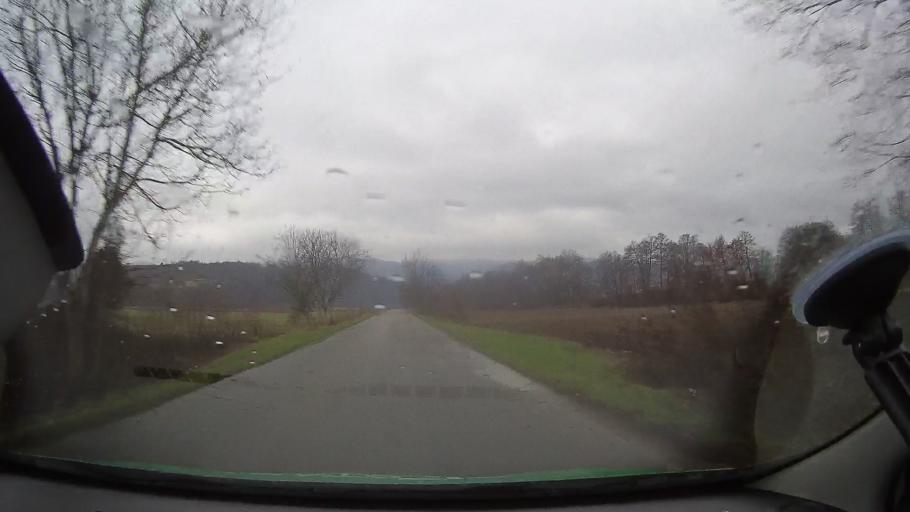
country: RO
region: Hunedoara
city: Vata de Jos
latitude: 46.1872
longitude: 22.6063
